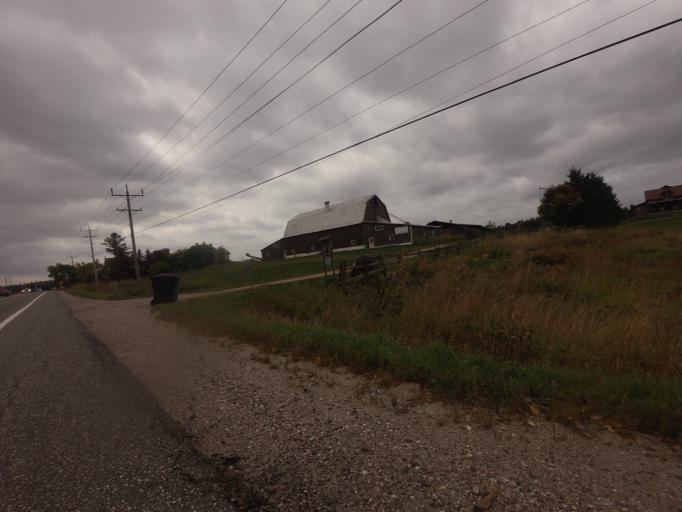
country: CA
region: Quebec
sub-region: Outaouais
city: Wakefield
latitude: 45.9146
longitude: -76.0171
